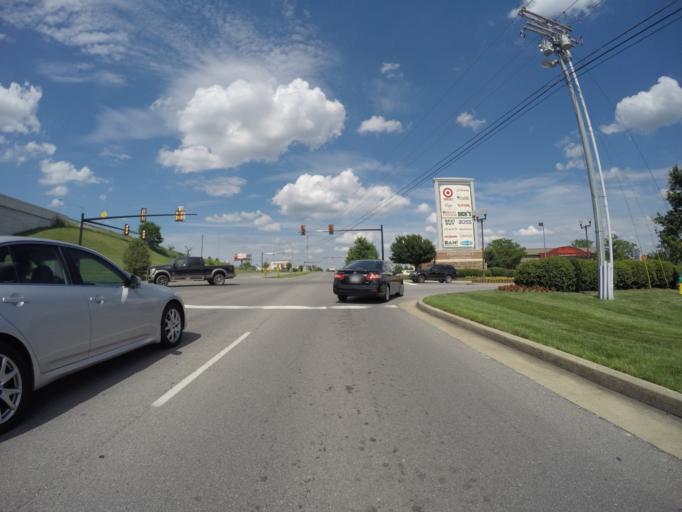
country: US
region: Tennessee
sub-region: Wilson County
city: Mount Juliet
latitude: 36.1697
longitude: -86.5108
